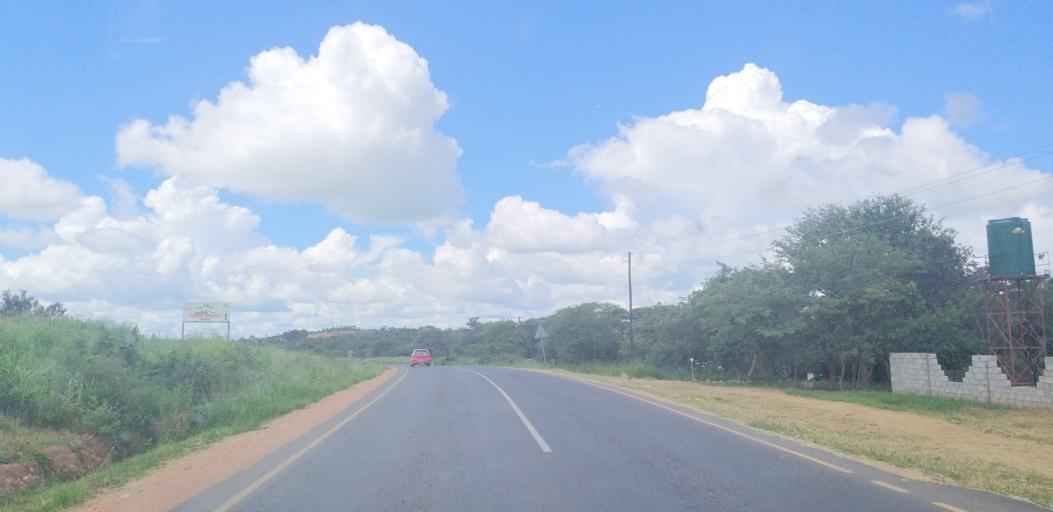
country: ZM
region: Lusaka
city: Lusaka
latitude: -15.3322
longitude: 28.3285
